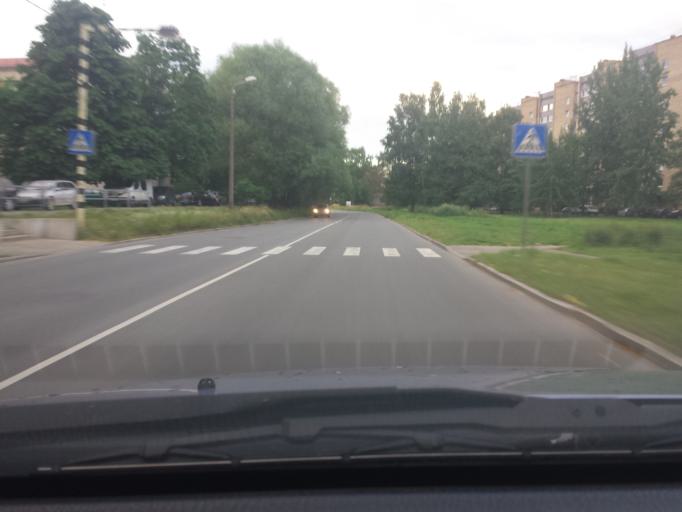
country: LV
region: Riga
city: Jaunciems
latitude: 56.9656
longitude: 24.1872
